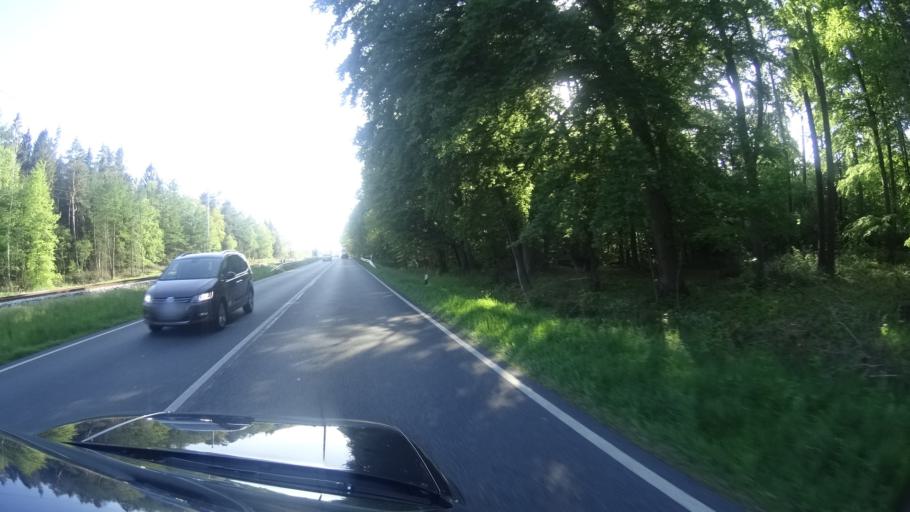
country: DE
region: Mecklenburg-Vorpommern
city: Rovershagen
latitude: 54.1858
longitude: 12.2712
